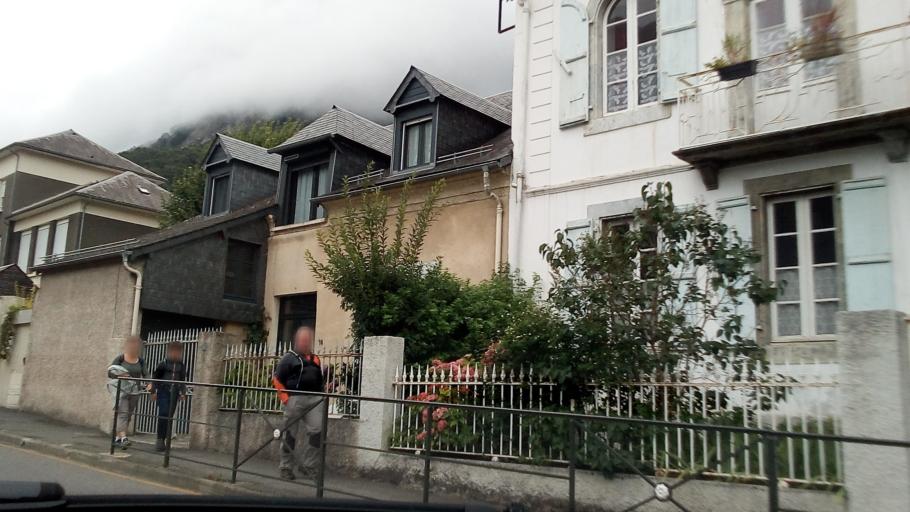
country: FR
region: Midi-Pyrenees
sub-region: Departement des Hautes-Pyrenees
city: Luz-Saint-Sauveur
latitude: 42.8723
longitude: -0.0020
